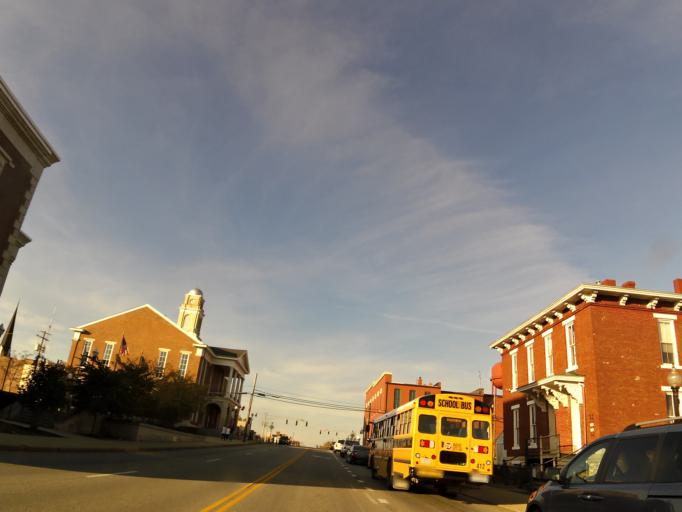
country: US
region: Kentucky
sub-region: Garrard County
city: Lancaster
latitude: 37.6181
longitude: -84.5789
